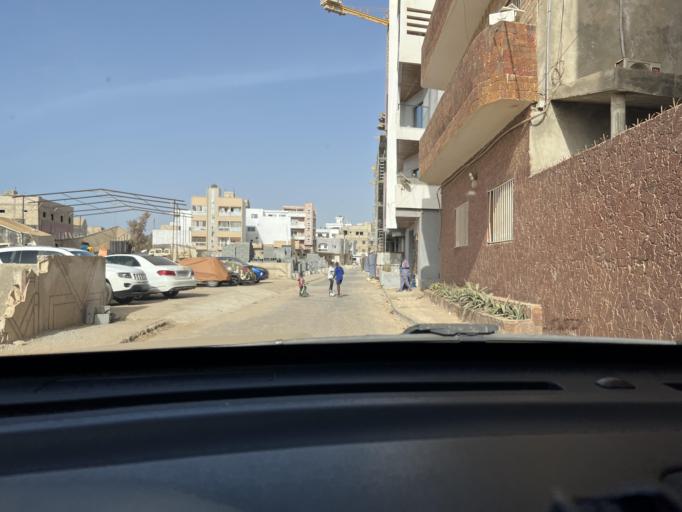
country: SN
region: Dakar
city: Mermoz Boabab
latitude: 14.7471
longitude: -17.5193
